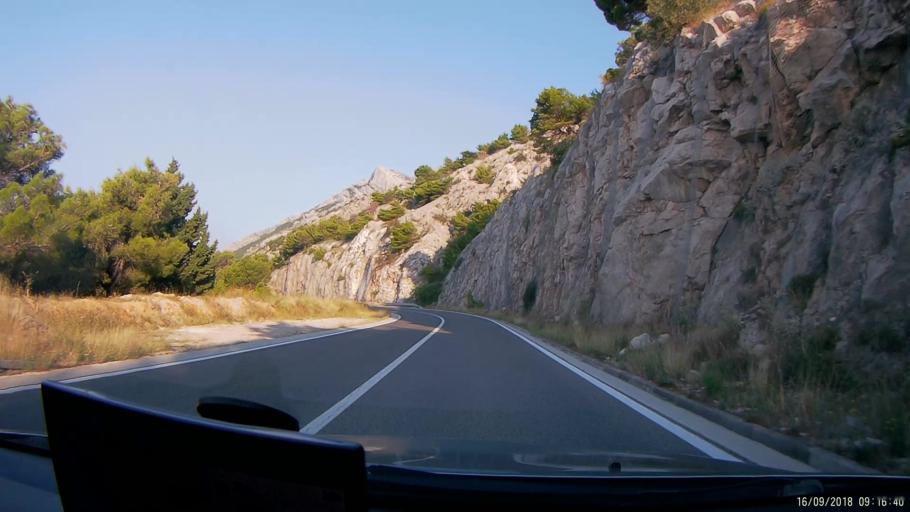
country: HR
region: Splitsko-Dalmatinska
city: Donja Brela
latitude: 43.4014
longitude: 16.8647
